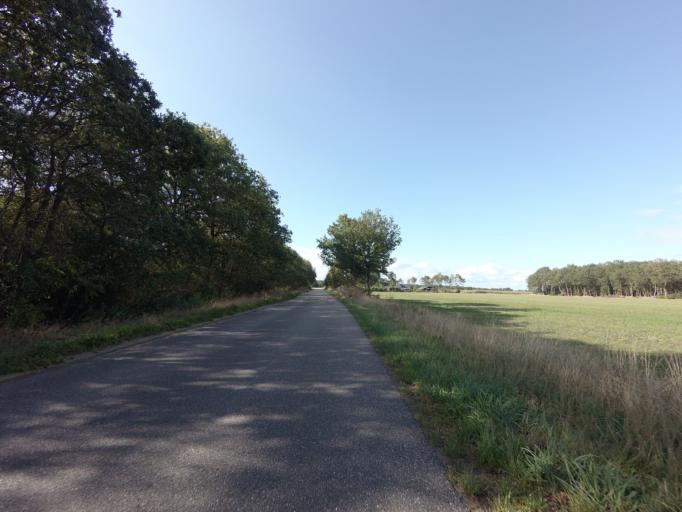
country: NL
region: Friesland
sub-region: Gemeente Heerenveen
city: Jubbega
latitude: 52.9736
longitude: 6.1895
